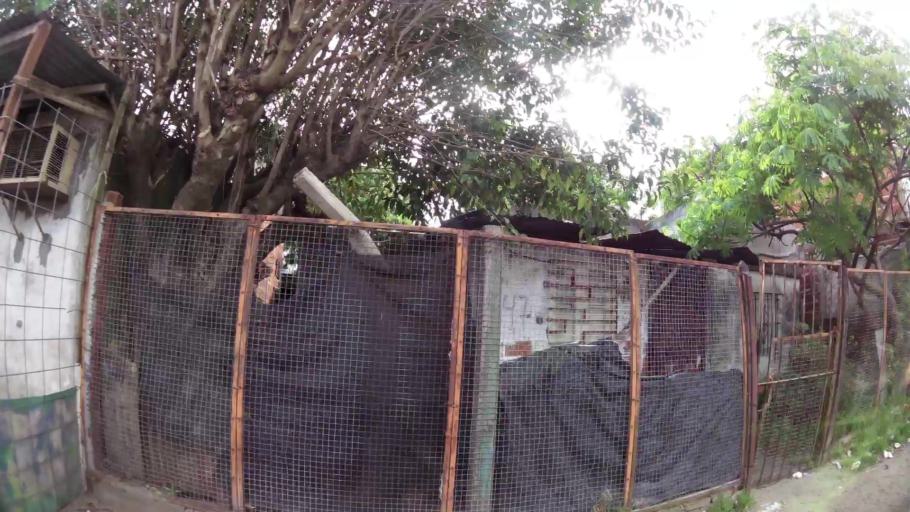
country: AR
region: Buenos Aires
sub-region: Partido de Quilmes
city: Quilmes
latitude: -34.7072
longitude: -58.2655
